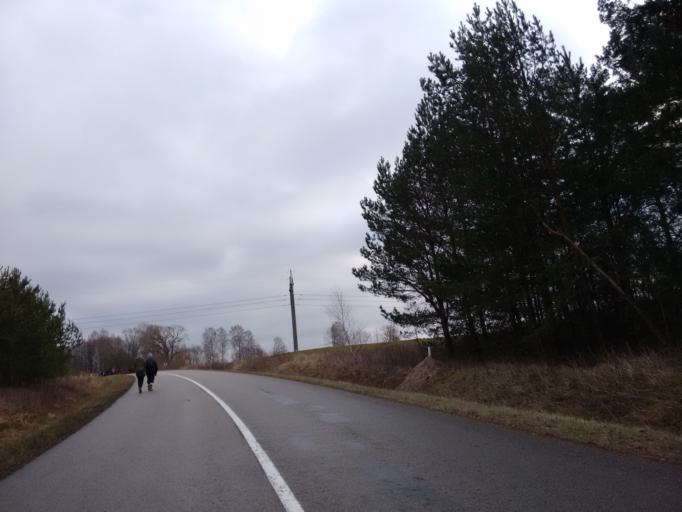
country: LT
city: Veisiejai
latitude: 54.2435
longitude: 23.8566
